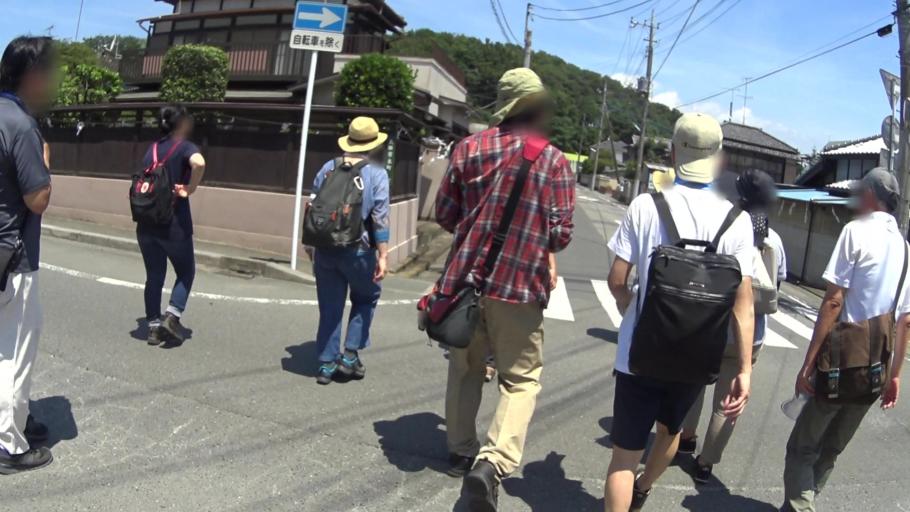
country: JP
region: Gunma
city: Ota
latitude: 36.2986
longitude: 139.3737
